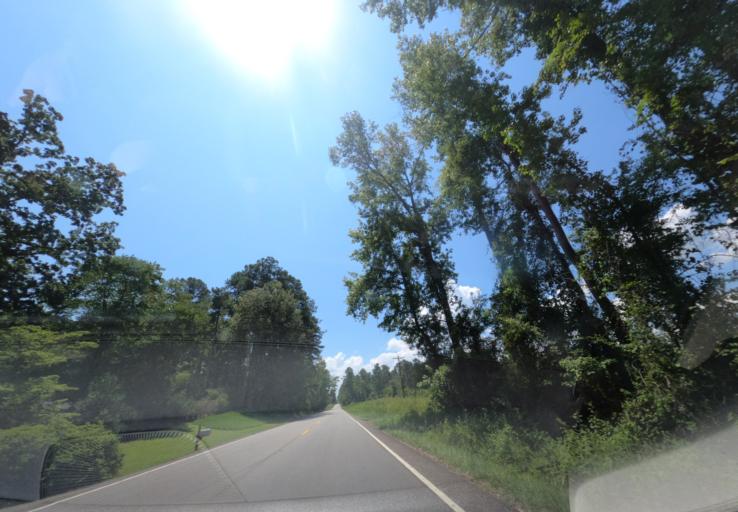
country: US
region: South Carolina
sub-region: Edgefield County
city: Murphys Estates
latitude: 33.5789
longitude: -82.0172
